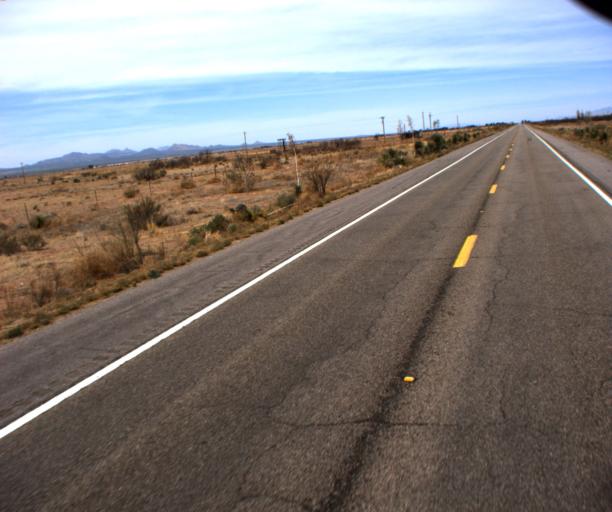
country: US
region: Arizona
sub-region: Cochise County
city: Pirtleville
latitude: 31.5672
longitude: -109.6678
